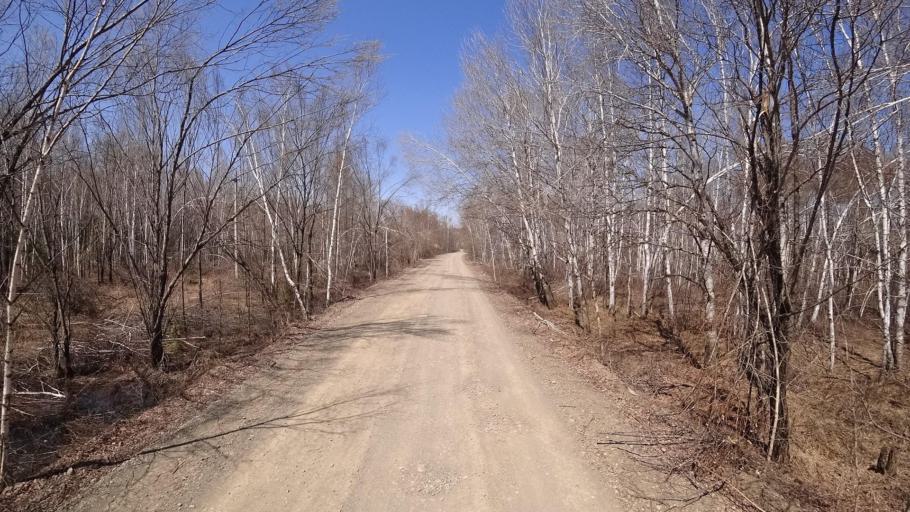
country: RU
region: Khabarovsk Krai
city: Khurba
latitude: 50.4155
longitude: 136.8390
